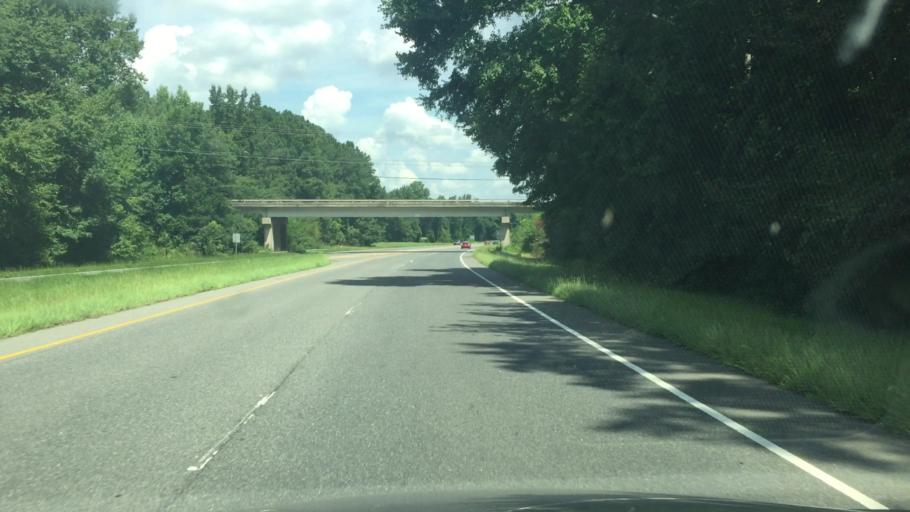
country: US
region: North Carolina
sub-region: Richmond County
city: Rockingham
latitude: 34.9309
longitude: -79.7804
